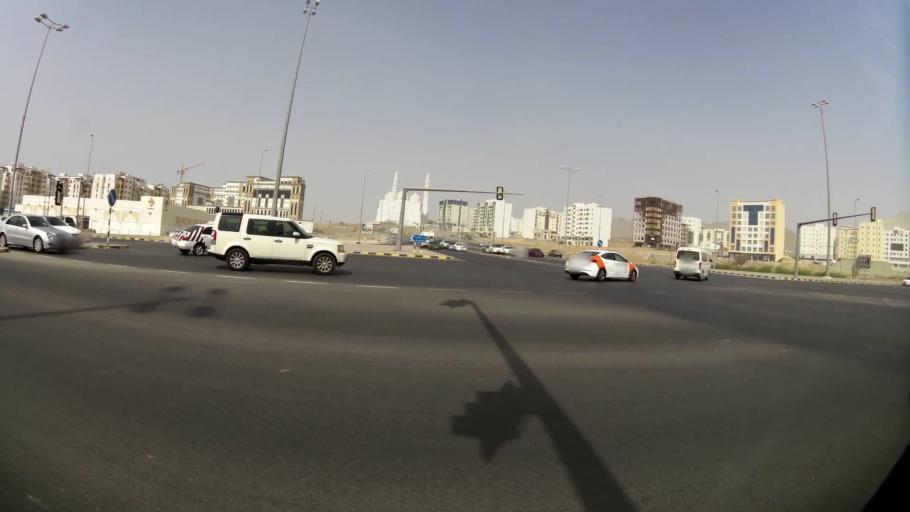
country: OM
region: Muhafazat Masqat
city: Bawshar
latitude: 23.5773
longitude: 58.4076
